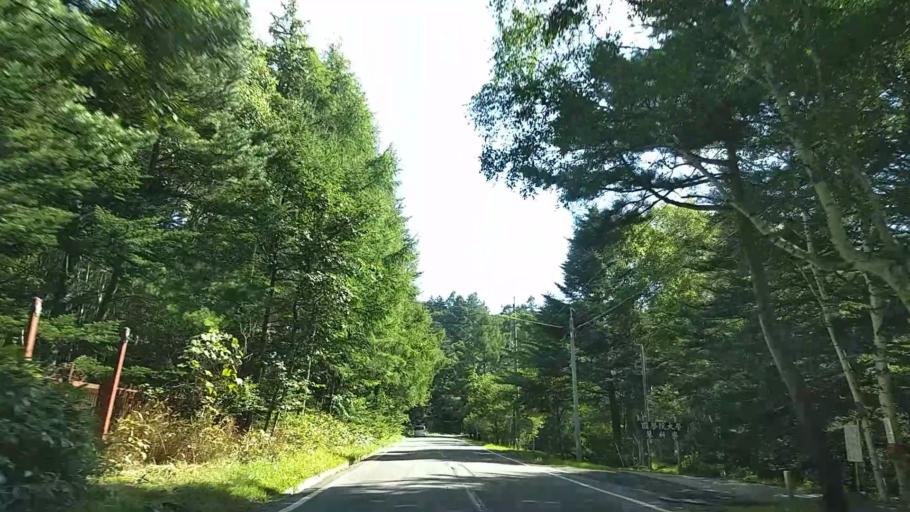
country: JP
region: Nagano
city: Chino
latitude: 36.1253
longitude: 138.2723
